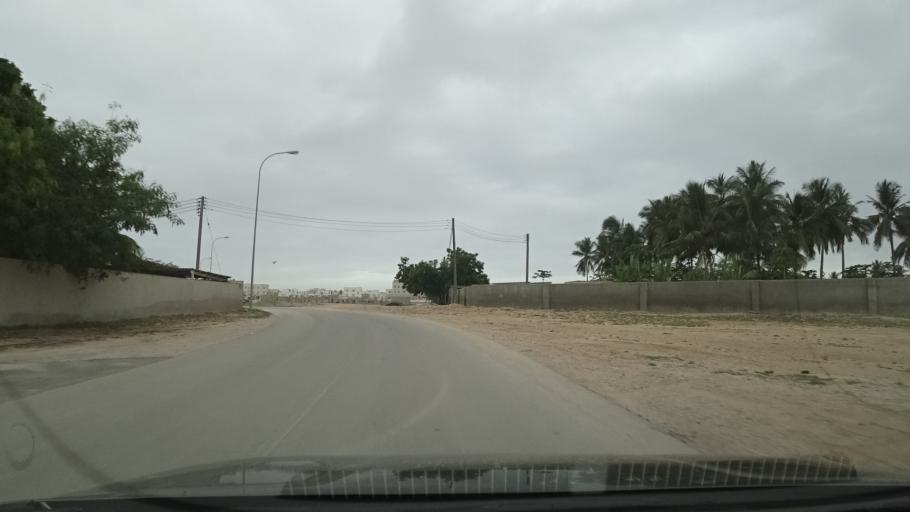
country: OM
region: Zufar
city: Salalah
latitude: 17.0244
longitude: 54.1539
